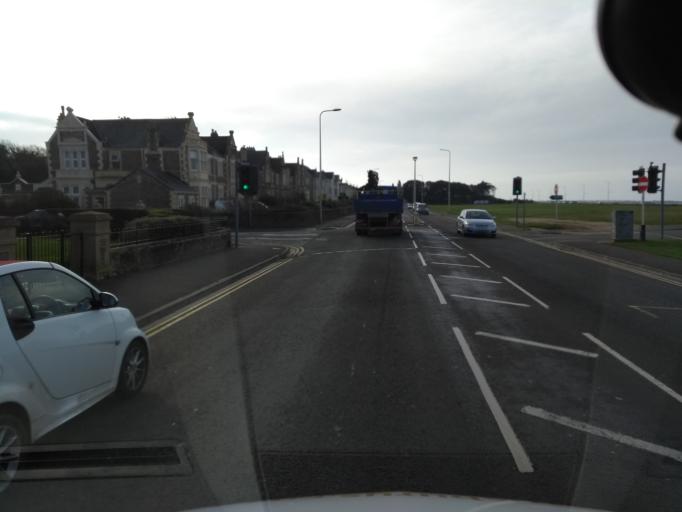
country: GB
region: England
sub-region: North Somerset
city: Weston-super-Mare
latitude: 51.3381
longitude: -2.9817
